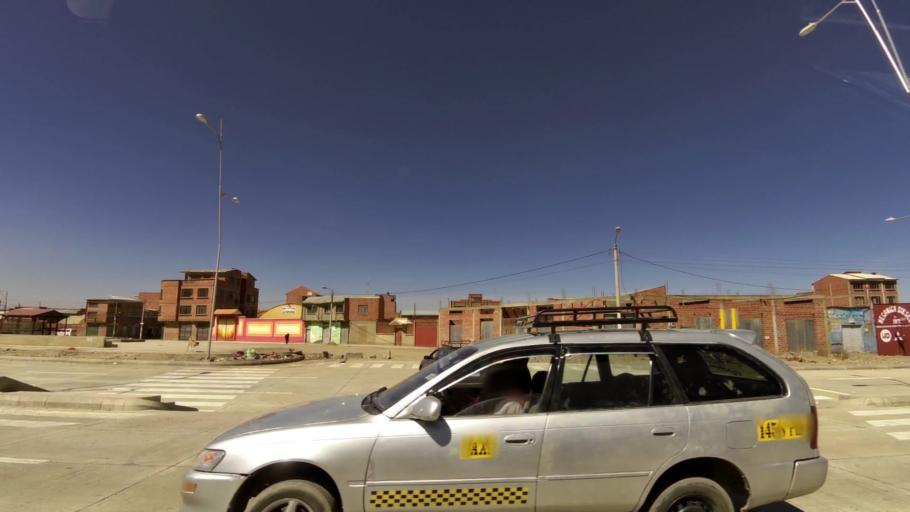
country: BO
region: La Paz
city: La Paz
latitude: -16.4945
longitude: -68.2206
